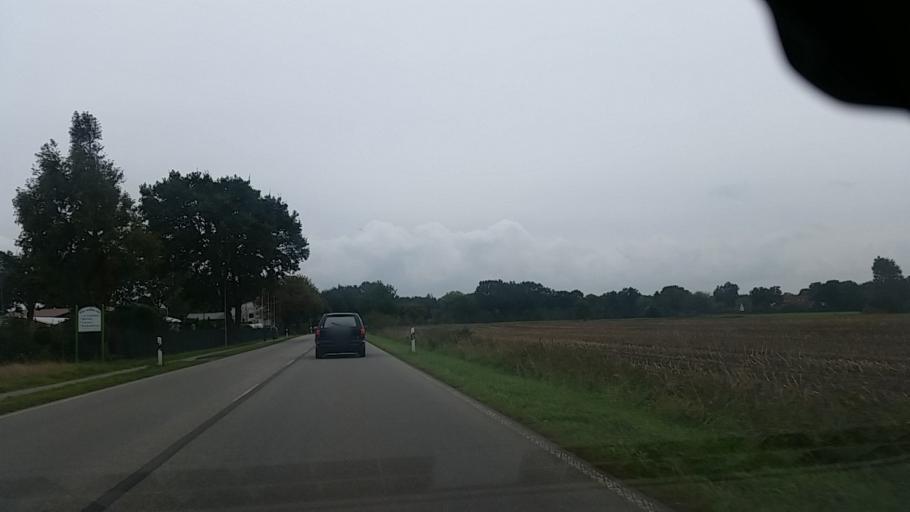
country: DE
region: Schleswig-Holstein
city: Kayhude
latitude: 53.7619
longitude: 10.1291
